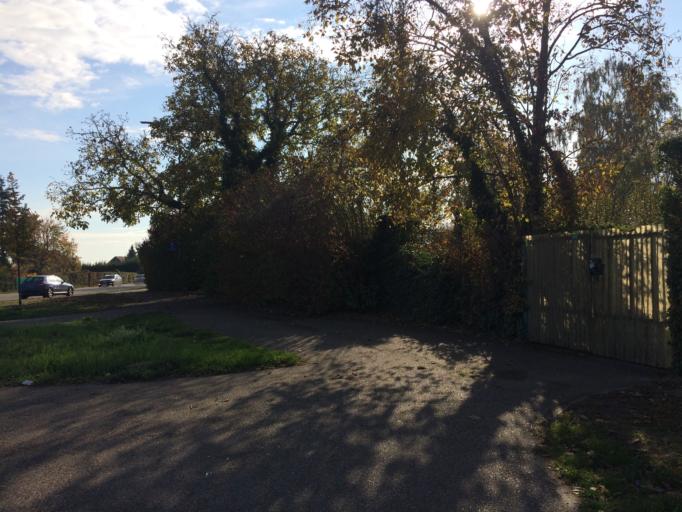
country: DE
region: Rheinland-Pfalz
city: Speyer
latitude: 49.3012
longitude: 8.4490
